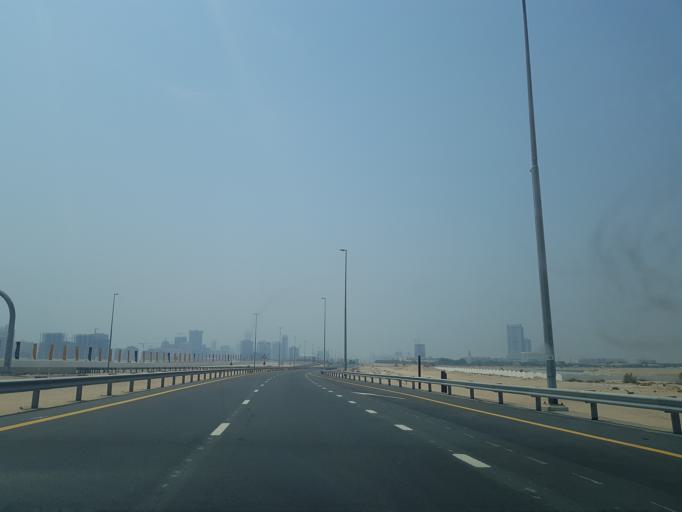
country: AE
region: Dubai
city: Dubai
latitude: 25.0264
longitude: 55.2383
